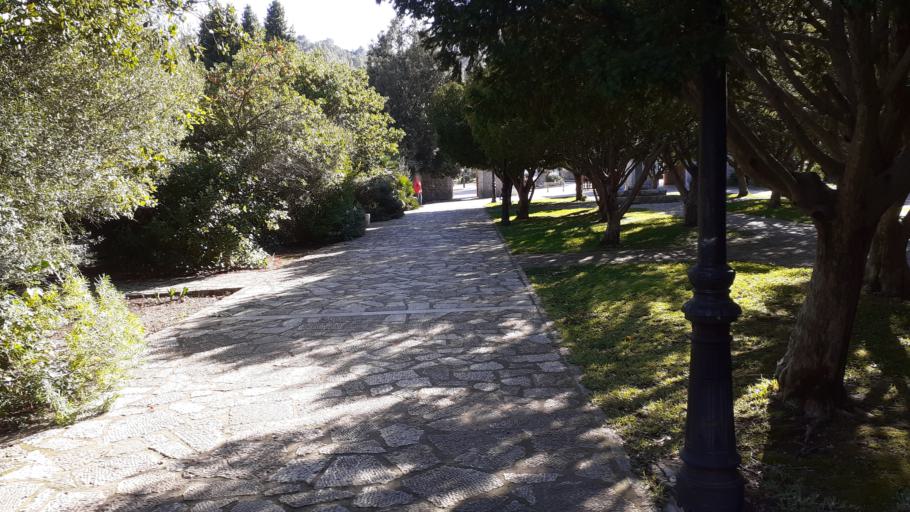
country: ES
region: Balearic Islands
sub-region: Illes Balears
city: Escorca
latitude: 39.8228
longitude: 2.8837
